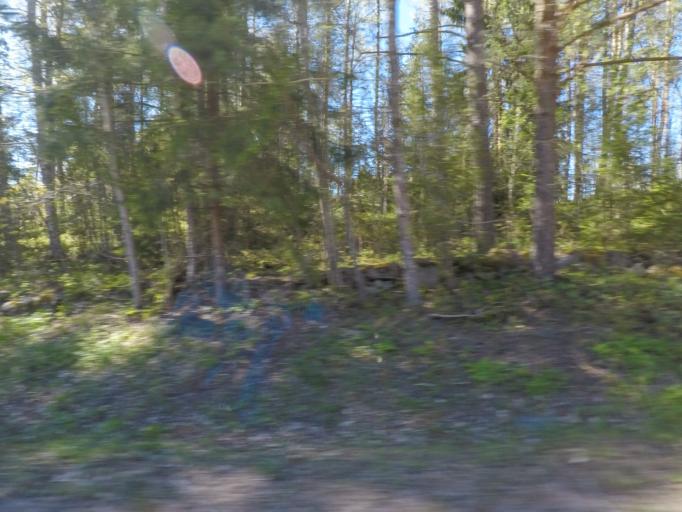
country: FI
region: Uusimaa
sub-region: Helsinki
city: Sammatti
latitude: 60.3520
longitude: 23.8004
